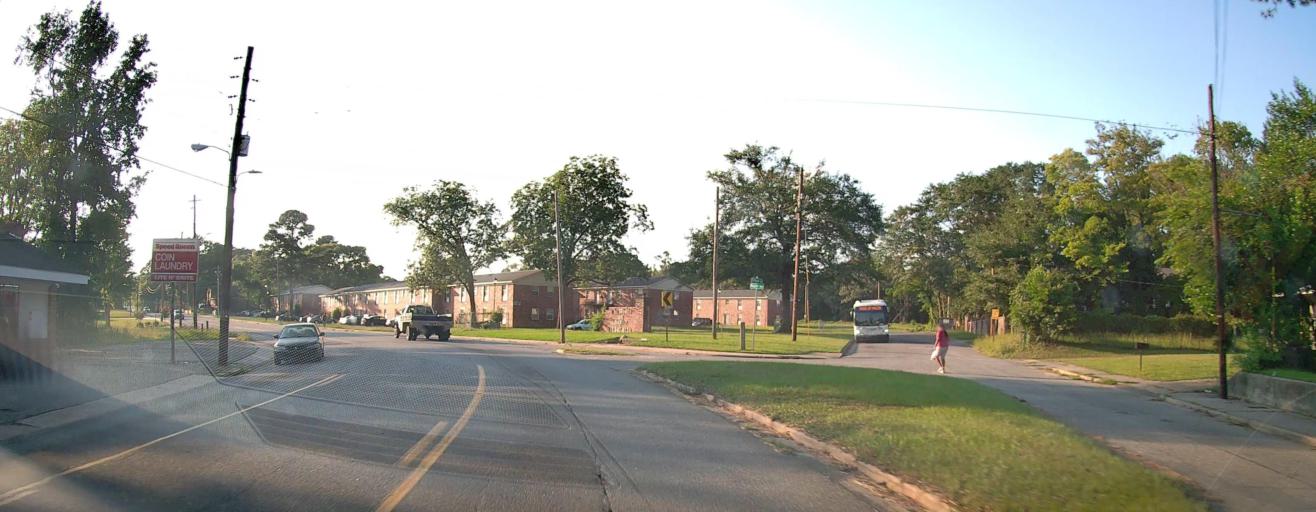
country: US
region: Georgia
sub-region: Bibb County
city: Macon
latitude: 32.8565
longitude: -83.6879
